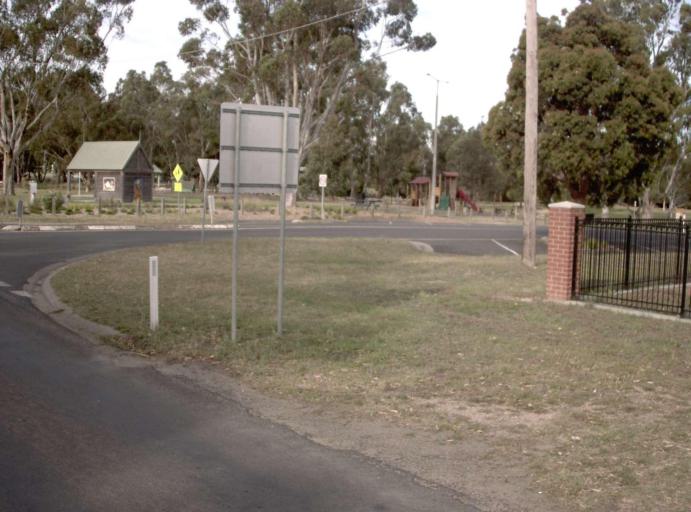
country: AU
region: Victoria
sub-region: Wellington
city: Heyfield
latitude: -37.9804
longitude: 146.7839
